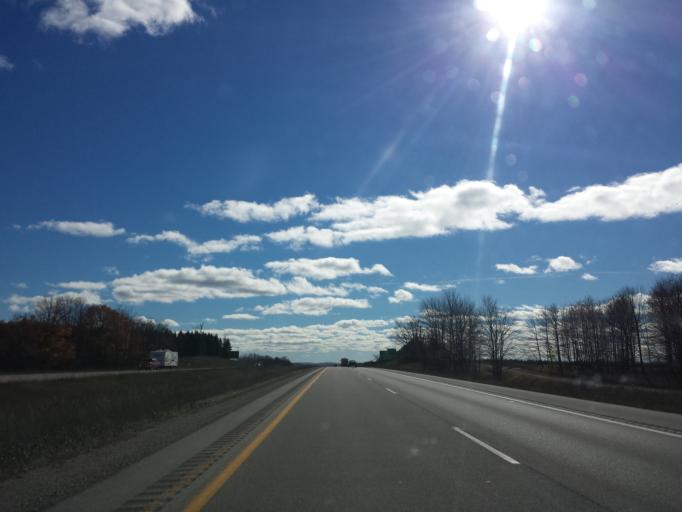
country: US
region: Michigan
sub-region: Cheboygan County
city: Cheboygan
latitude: 45.5850
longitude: -84.6209
